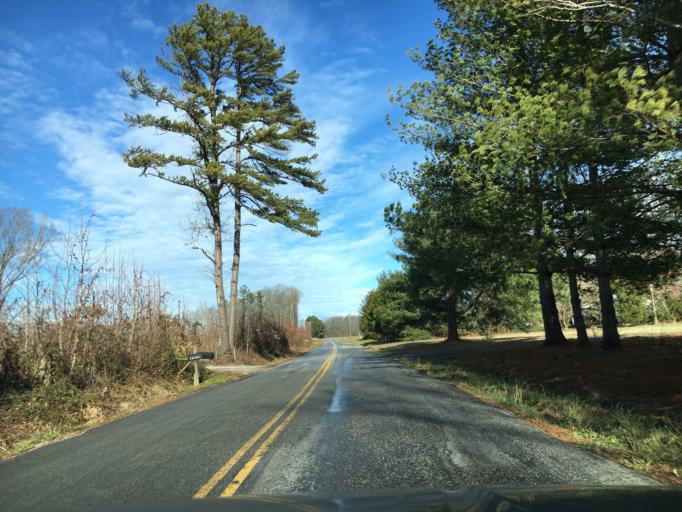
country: US
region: Virginia
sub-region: Cumberland County
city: Cumberland
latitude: 37.3608
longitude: -78.1557
